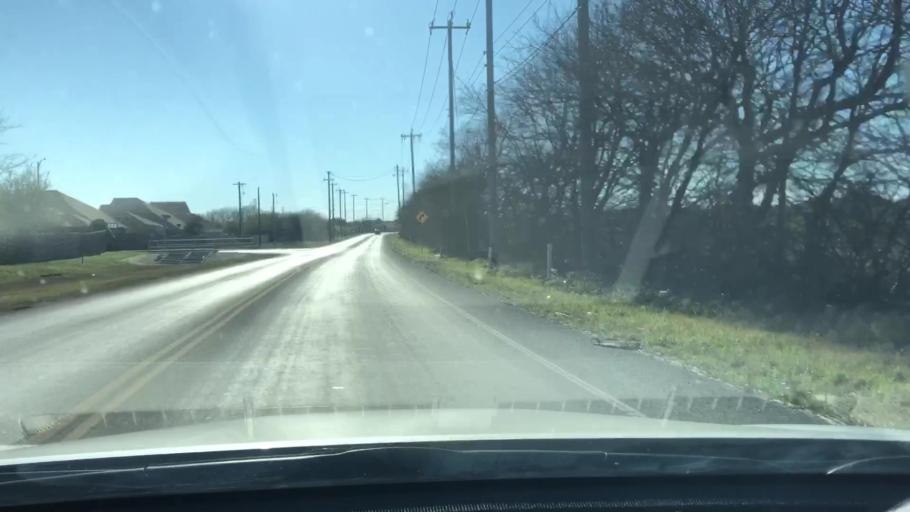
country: US
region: Texas
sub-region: Bexar County
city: Converse
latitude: 29.4729
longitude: -98.3174
